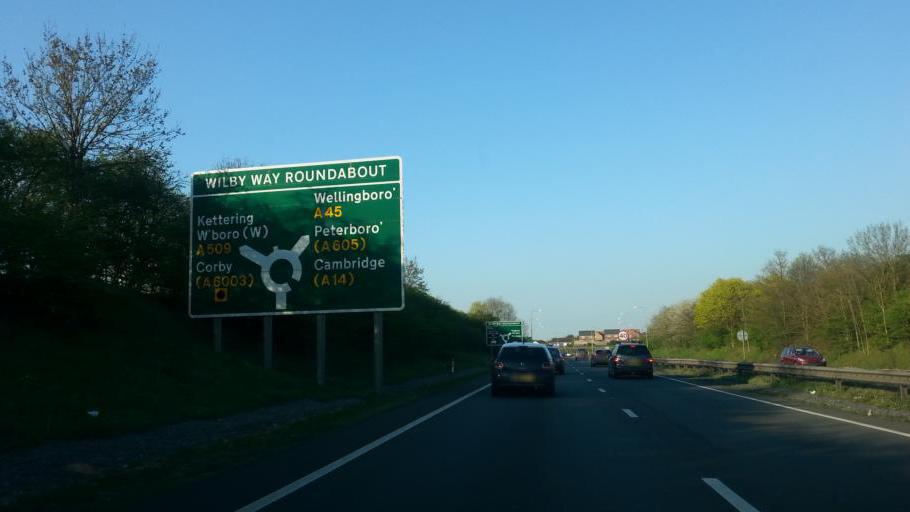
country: GB
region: England
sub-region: Northamptonshire
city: Wellingborough
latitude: 52.2813
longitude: -0.7149
